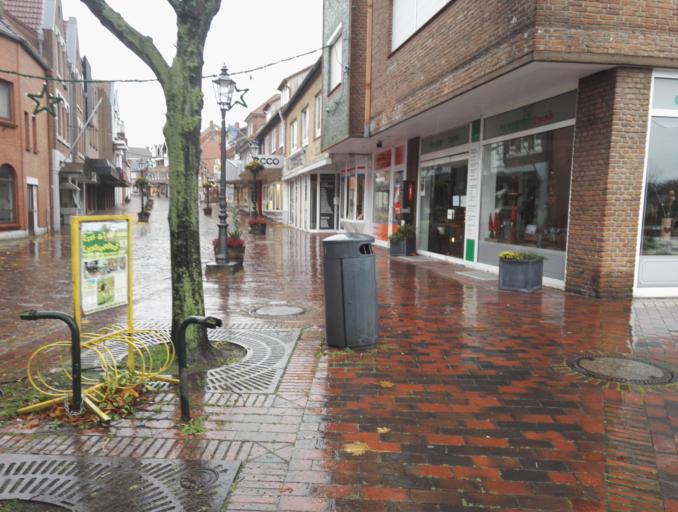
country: DE
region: Schleswig-Holstein
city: Oldenburg in Holstein
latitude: 54.2913
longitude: 10.8898
